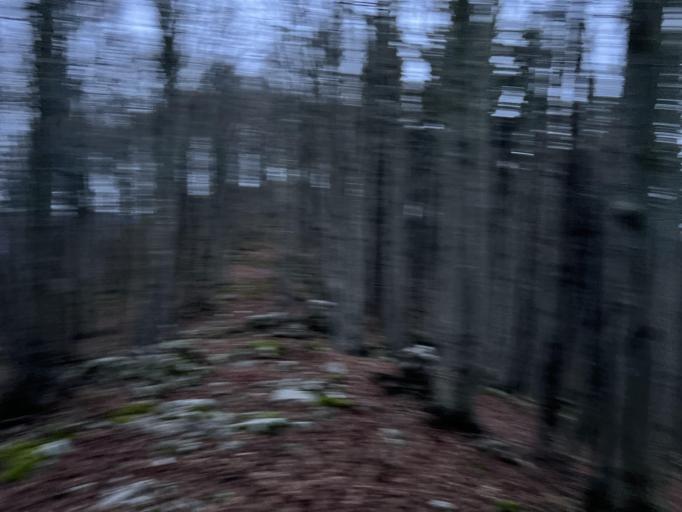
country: SI
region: Ajdovscina
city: Lokavec
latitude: 45.9517
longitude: 13.8352
